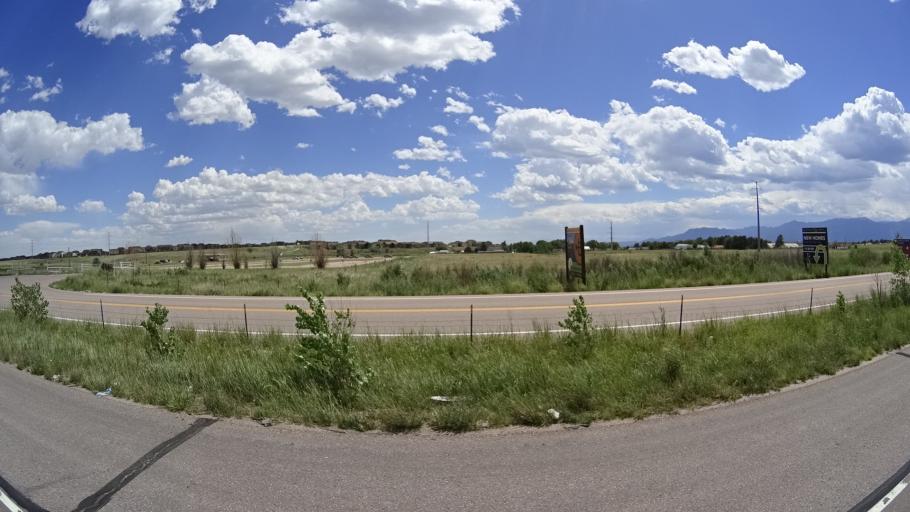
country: US
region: Colorado
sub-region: El Paso County
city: Black Forest
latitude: 38.9412
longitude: -104.6851
